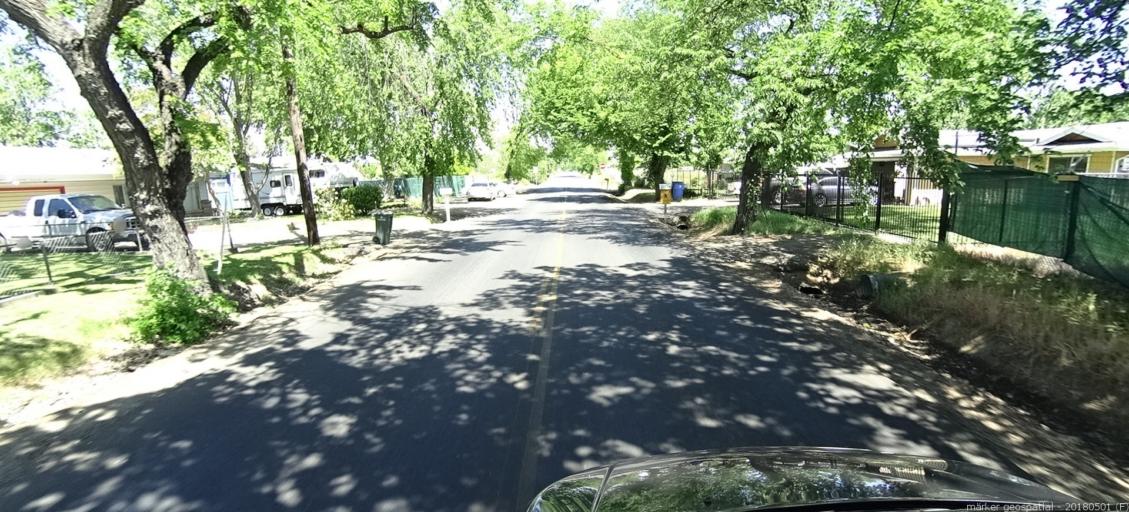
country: US
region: California
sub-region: Sacramento County
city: Rio Linda
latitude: 38.6611
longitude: -121.4384
